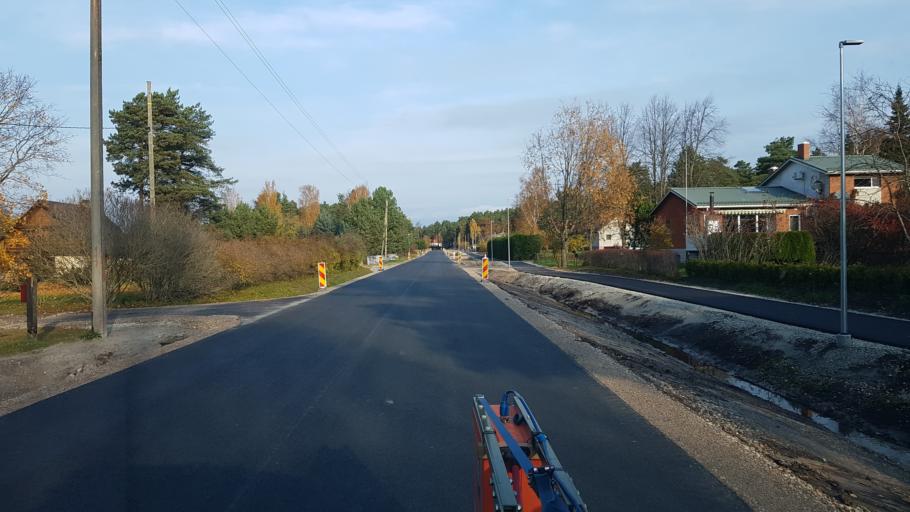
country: EE
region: Paernumaa
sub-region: Paikuse vald
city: Paikuse
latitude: 58.3498
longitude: 24.6207
